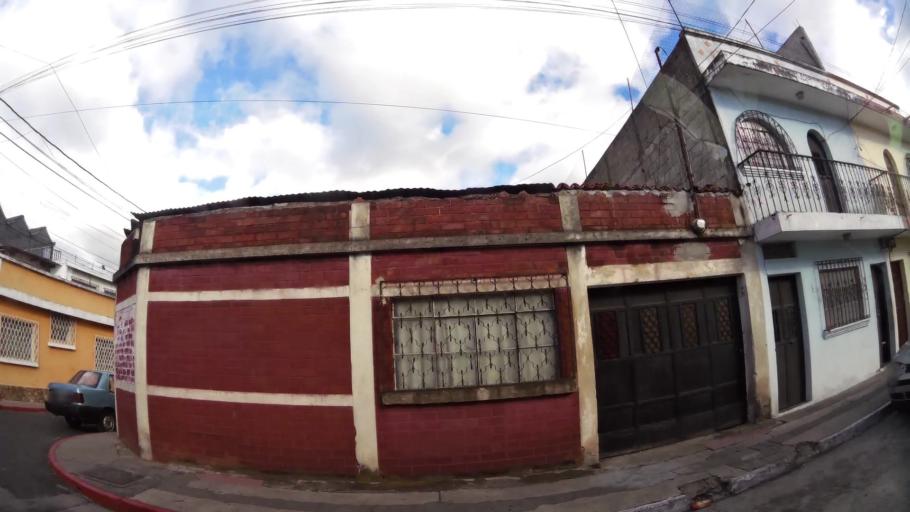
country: GT
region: Guatemala
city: Guatemala City
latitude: 14.6358
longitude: -90.5017
